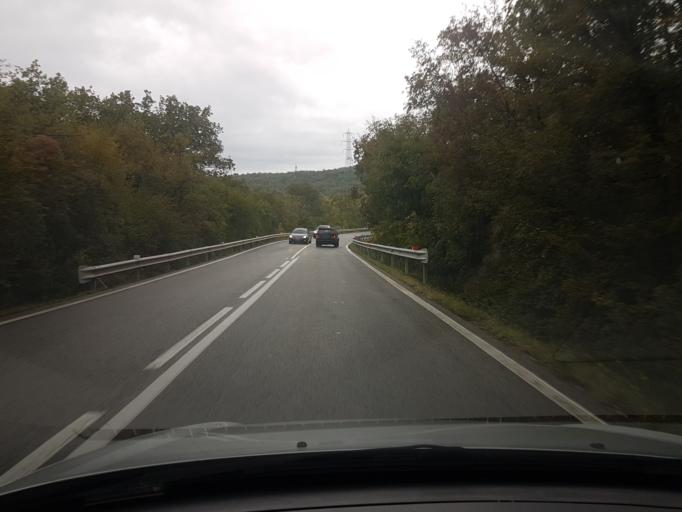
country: IT
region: Friuli Venezia Giulia
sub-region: Provincia di Gorizia
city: Monfalcone
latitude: 45.8138
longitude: 13.5743
